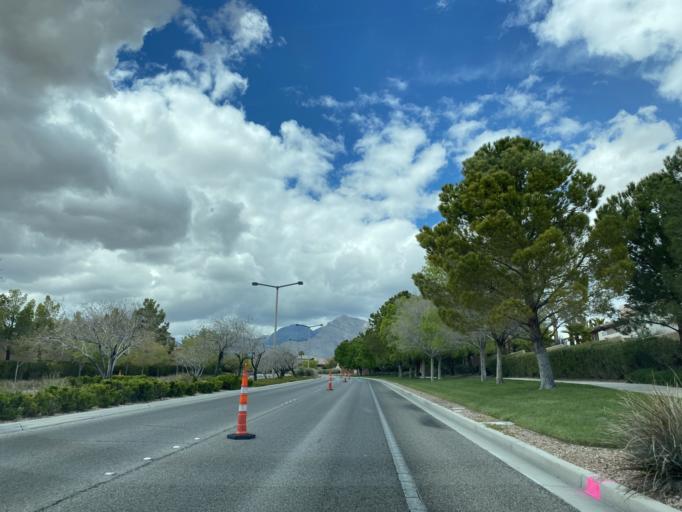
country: US
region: Nevada
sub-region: Clark County
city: Summerlin South
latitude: 36.1721
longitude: -115.3459
